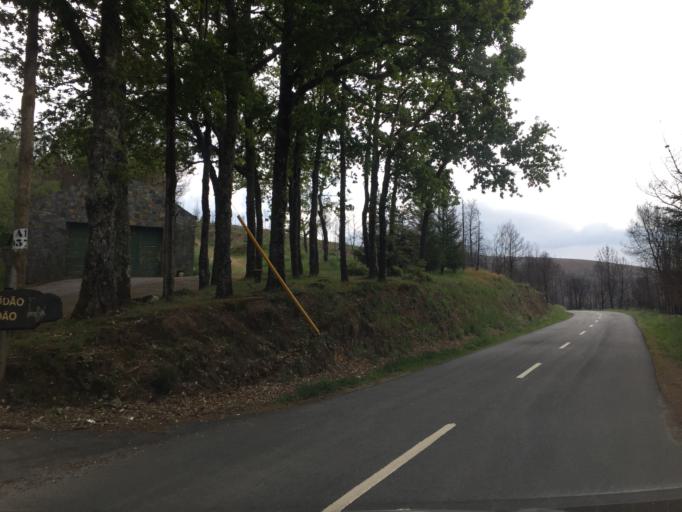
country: PT
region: Coimbra
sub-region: Arganil
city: Arganil
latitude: 40.1852
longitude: -7.9754
